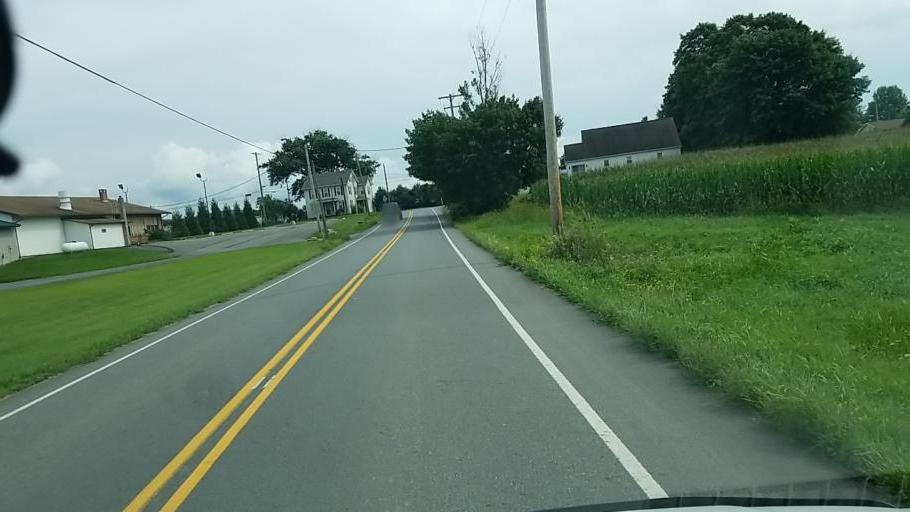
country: US
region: Pennsylvania
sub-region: Dauphin County
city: Elizabethville
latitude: 40.6076
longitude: -76.7788
